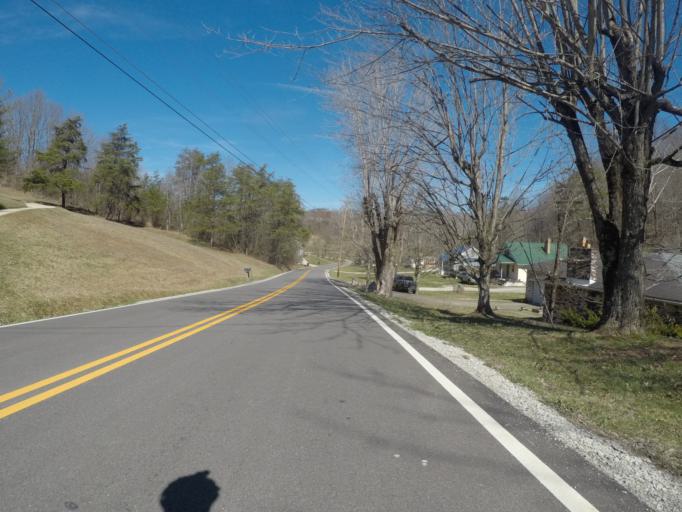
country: US
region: Ohio
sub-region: Lawrence County
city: Burlington
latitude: 38.4554
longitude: -82.5378
